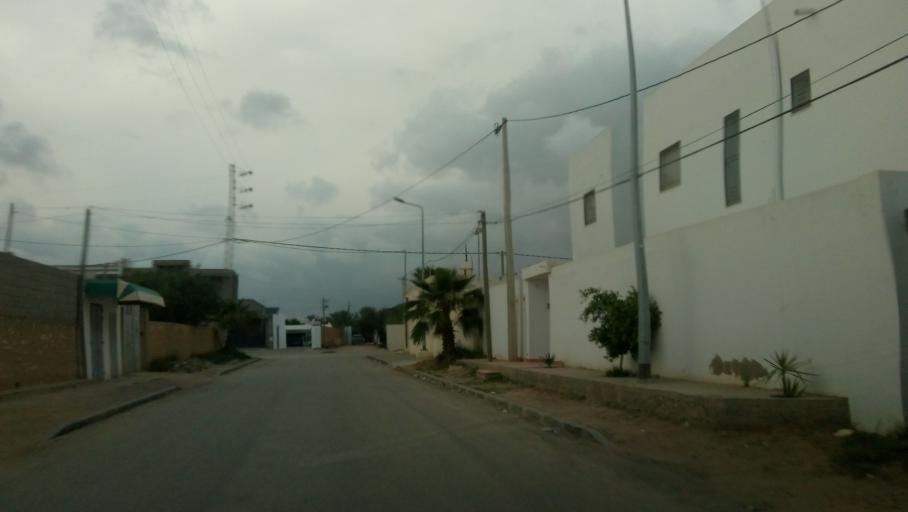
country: TN
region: Safaqis
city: Sfax
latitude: 34.7696
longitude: 10.7008
